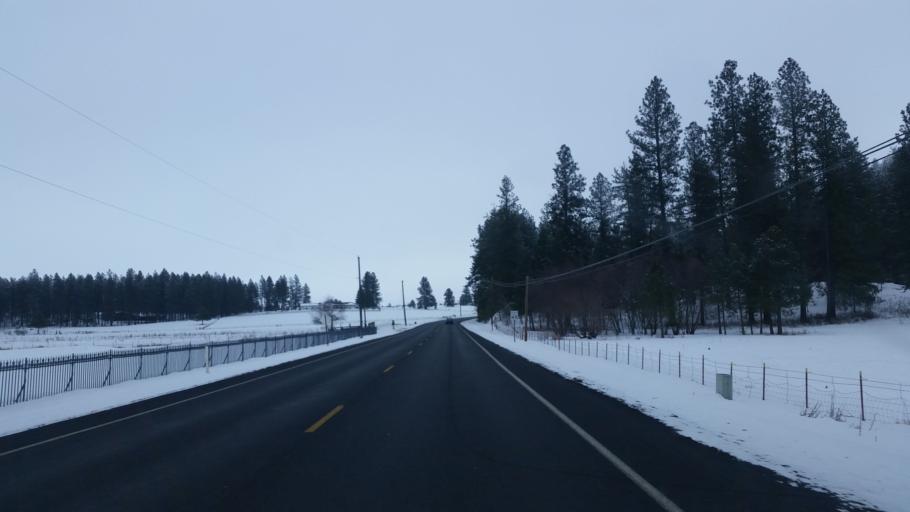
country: US
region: Washington
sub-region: Spokane County
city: Medical Lake
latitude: 47.5746
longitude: -117.6413
